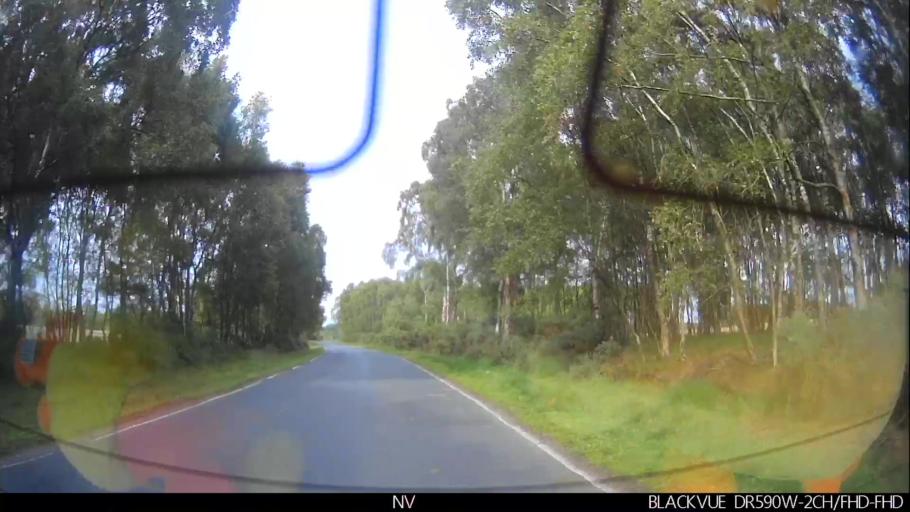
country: GB
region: England
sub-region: North Yorkshire
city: Strensall
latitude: 54.0436
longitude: -1.0100
